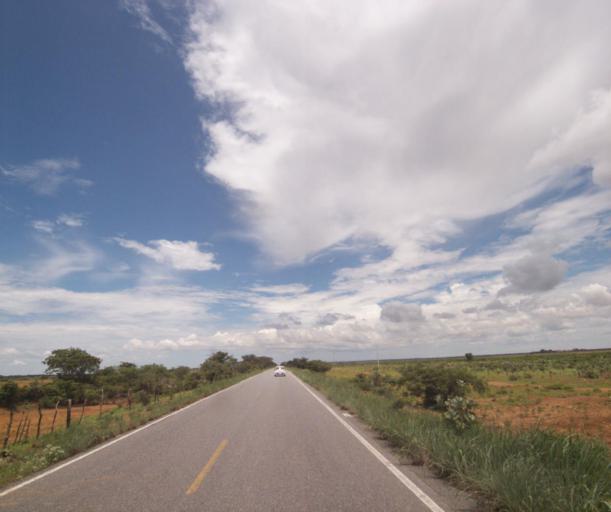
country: BR
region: Bahia
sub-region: Carinhanha
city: Carinhanha
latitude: -14.2897
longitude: -43.6465
